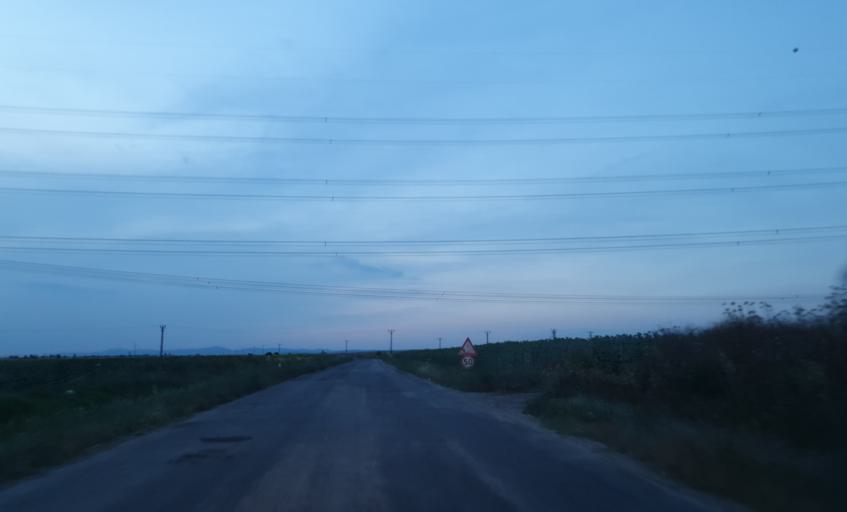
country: TR
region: Kirklareli
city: Vize
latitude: 41.4943
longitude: 27.7519
